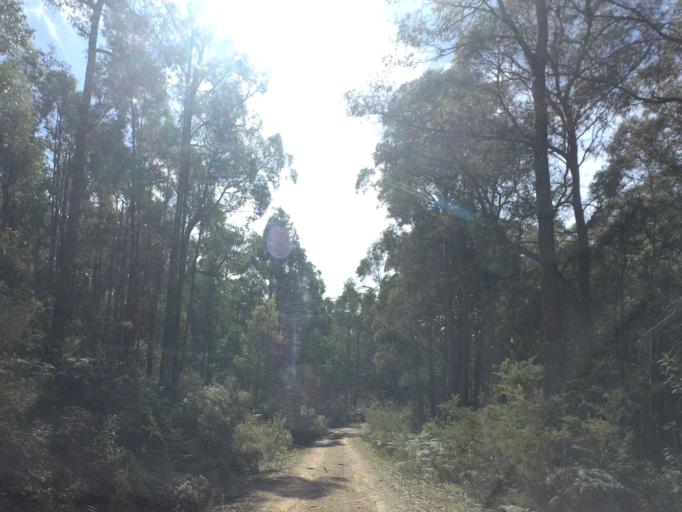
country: AU
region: Victoria
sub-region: Moorabool
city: Bacchus Marsh
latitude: -37.4379
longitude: 144.2736
